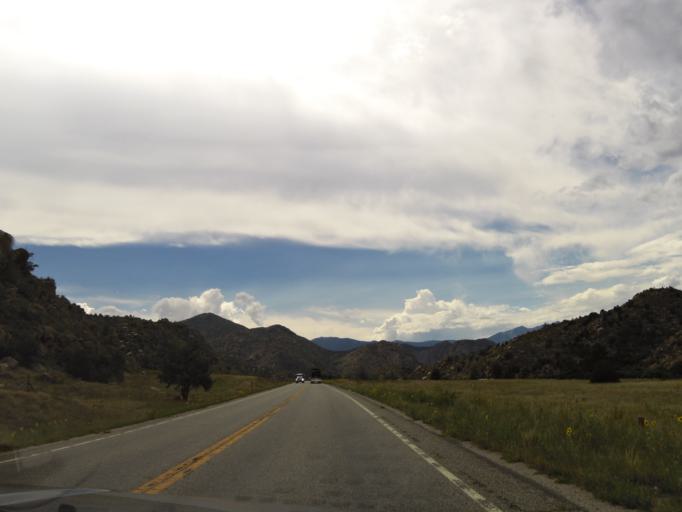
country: US
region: Colorado
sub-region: Custer County
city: Westcliffe
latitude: 38.3835
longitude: -105.6618
